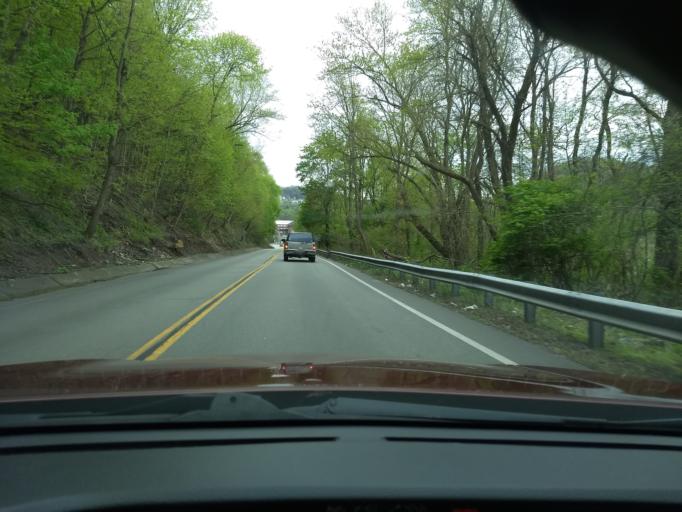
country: US
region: Pennsylvania
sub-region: Allegheny County
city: Wilmerding
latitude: 40.3923
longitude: -79.8012
